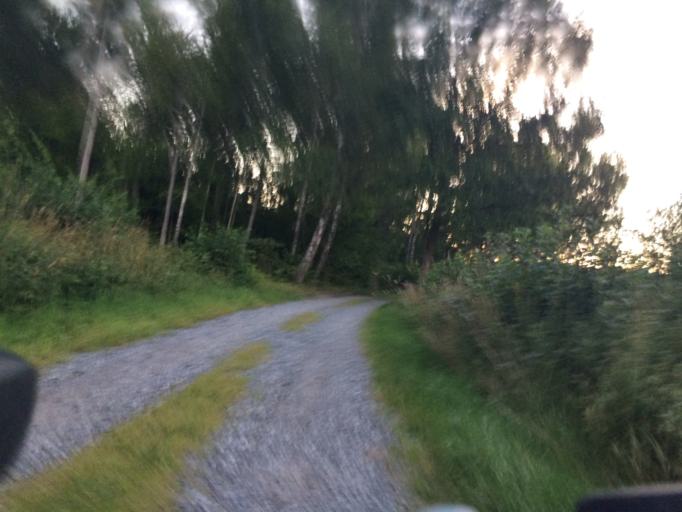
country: SE
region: Soedermanland
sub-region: Eskilstuna Kommun
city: Kvicksund
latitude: 59.4473
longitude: 16.3103
